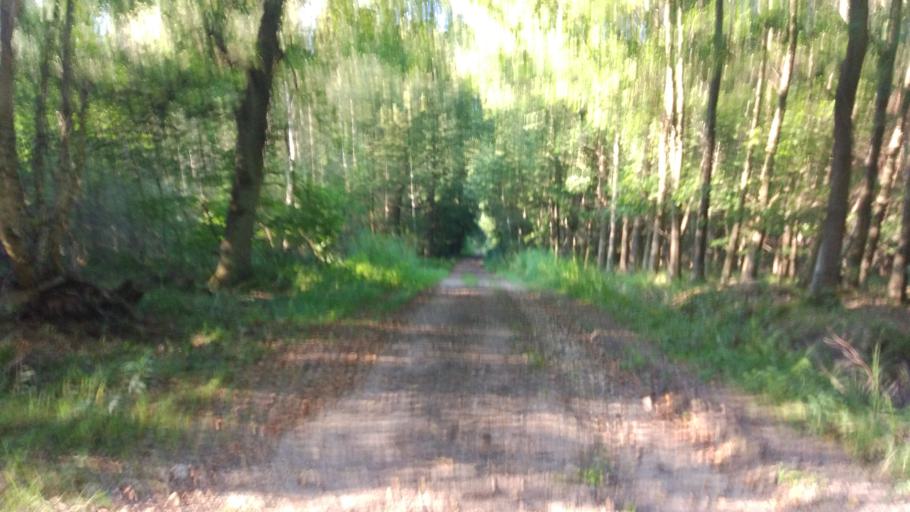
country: FR
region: Alsace
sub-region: Departement du Bas-Rhin
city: Gries
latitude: 48.7680
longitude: 7.8217
